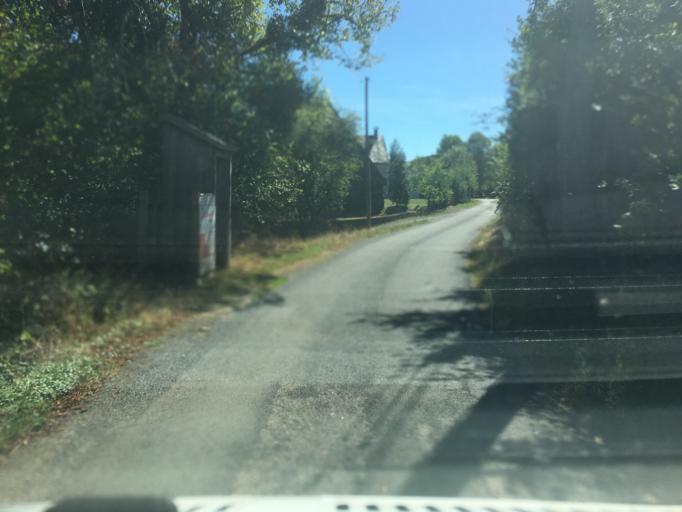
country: FR
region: Limousin
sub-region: Departement de la Correze
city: Bort-les-Orgues
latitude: 45.4394
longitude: 2.4864
